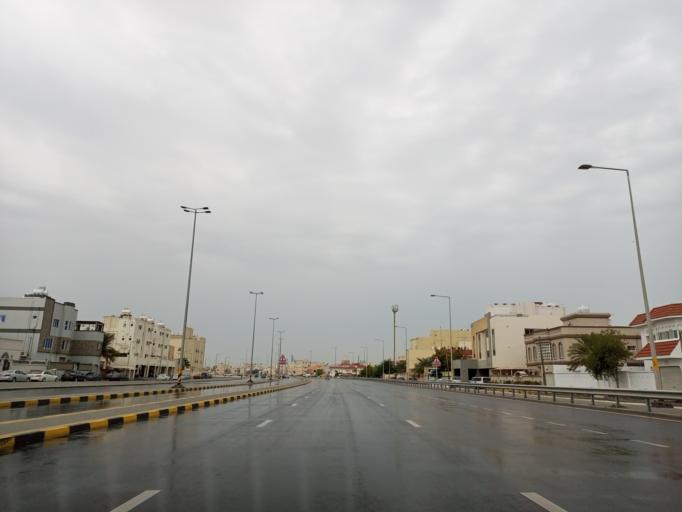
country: BH
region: Muharraq
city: Al Hadd
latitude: 26.2475
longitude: 50.6439
